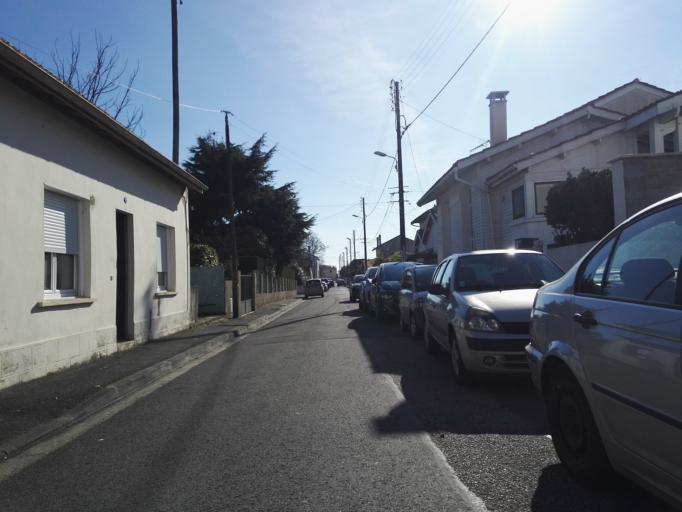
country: FR
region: Aquitaine
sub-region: Departement de la Gironde
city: Merignac
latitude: 44.8310
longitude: -0.6223
